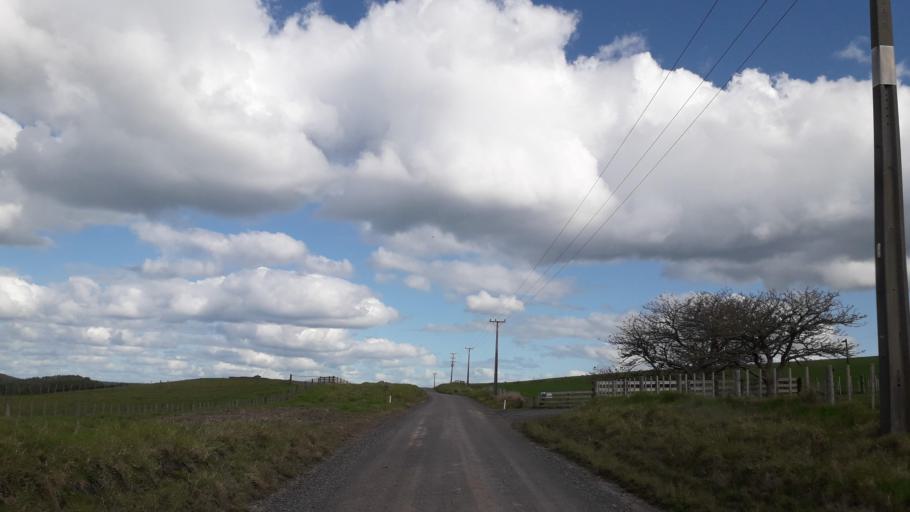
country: NZ
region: Northland
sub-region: Far North District
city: Kerikeri
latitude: -35.1438
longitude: 174.0374
